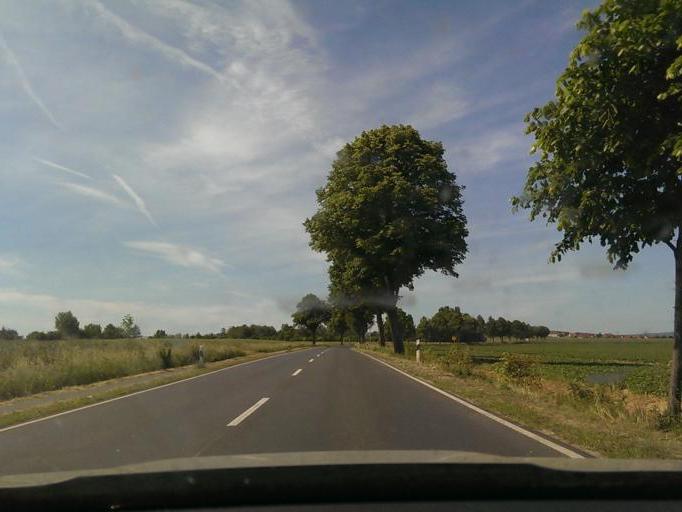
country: DE
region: Lower Saxony
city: Elze
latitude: 52.1406
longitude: 9.7577
